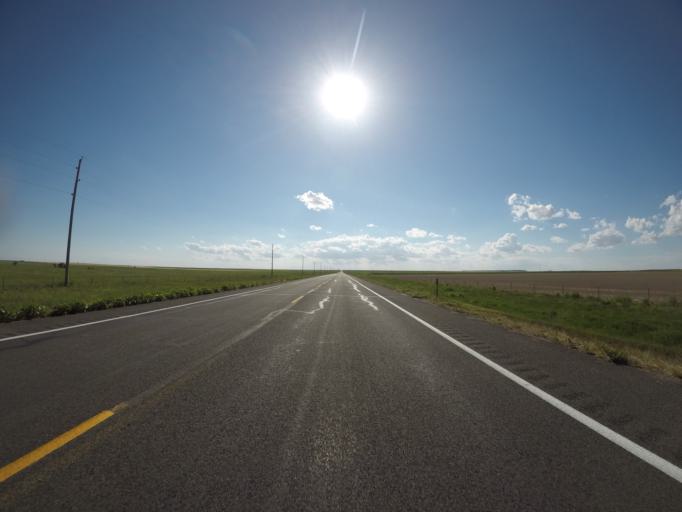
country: US
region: Colorado
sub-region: Morgan County
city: Fort Morgan
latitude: 40.6105
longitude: -103.7411
